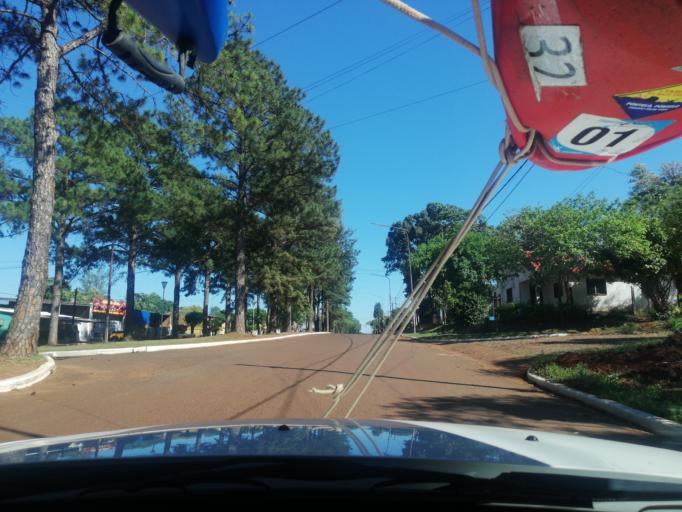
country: AR
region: Misiones
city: Santa Ana
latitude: -27.3727
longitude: -55.5785
